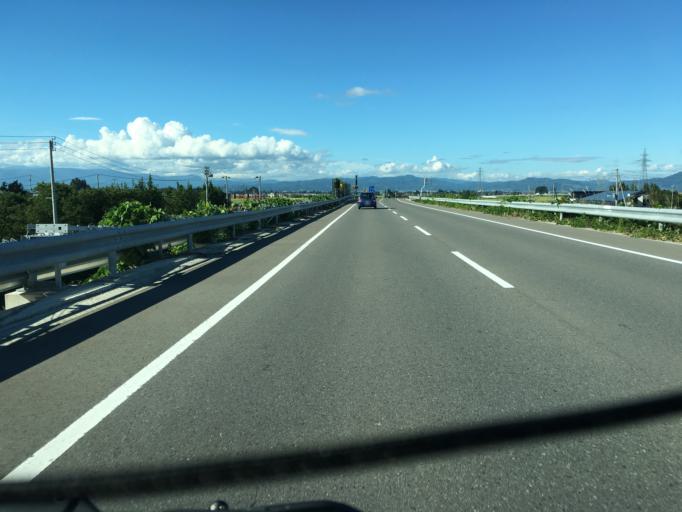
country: JP
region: Yamagata
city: Yonezawa
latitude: 37.9472
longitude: 140.1119
